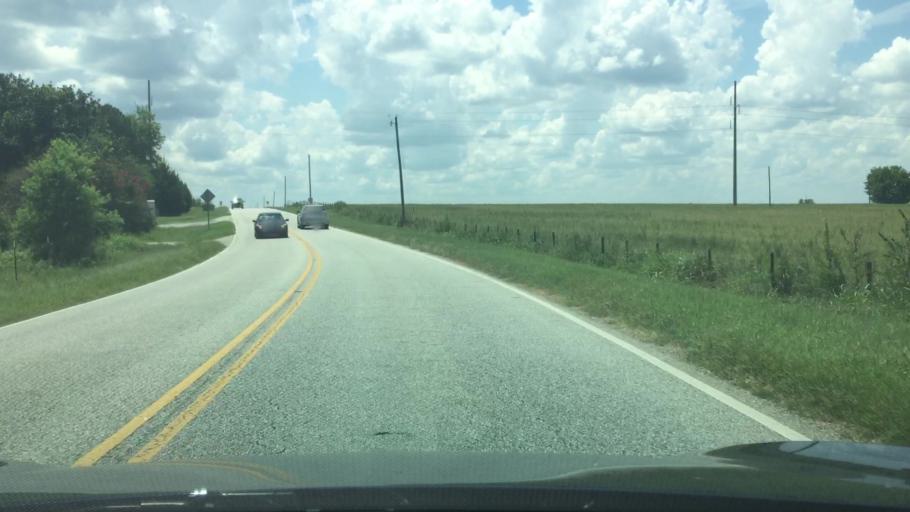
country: US
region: Alabama
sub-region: Montgomery County
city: Pike Road
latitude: 32.2805
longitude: -86.1025
